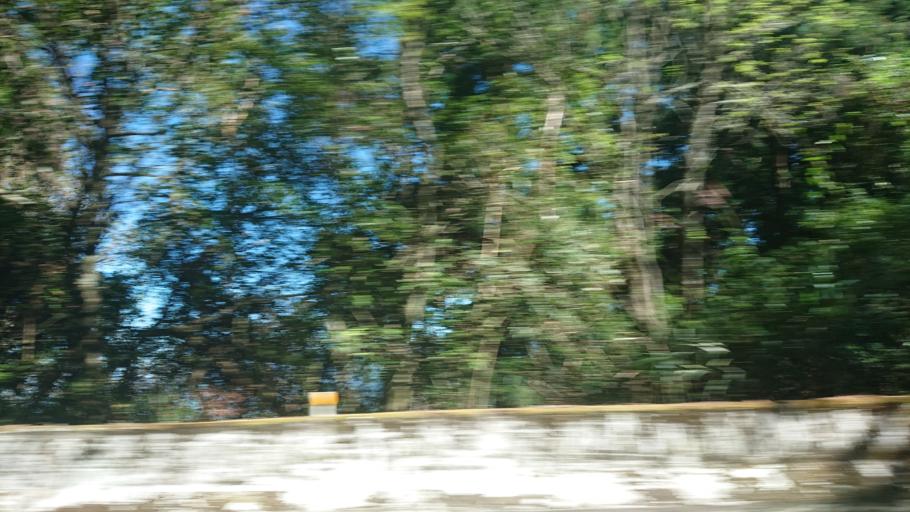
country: TW
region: Taiwan
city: Lugu
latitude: 23.4775
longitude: 120.8373
